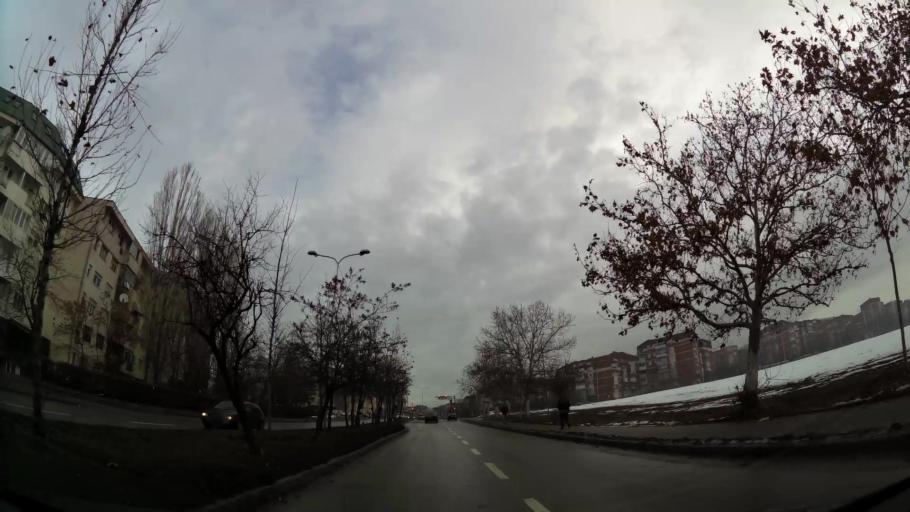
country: XK
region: Pristina
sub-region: Komuna e Prishtines
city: Pristina
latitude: 42.6493
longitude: 21.1642
